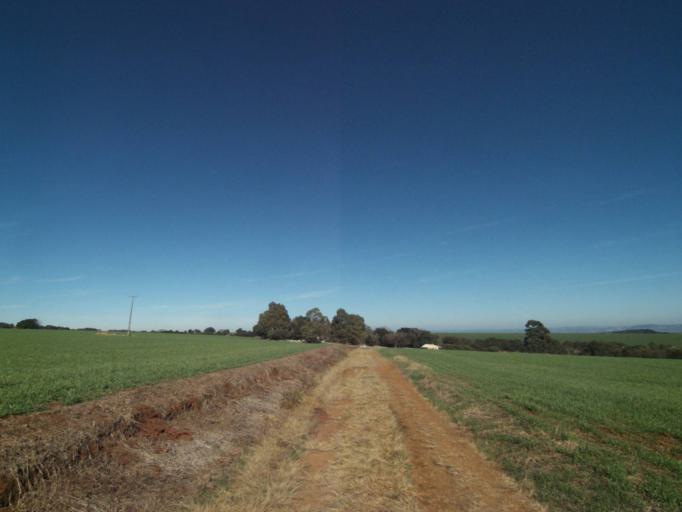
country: BR
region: Parana
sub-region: Tibagi
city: Tibagi
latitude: -24.5476
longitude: -50.2979
